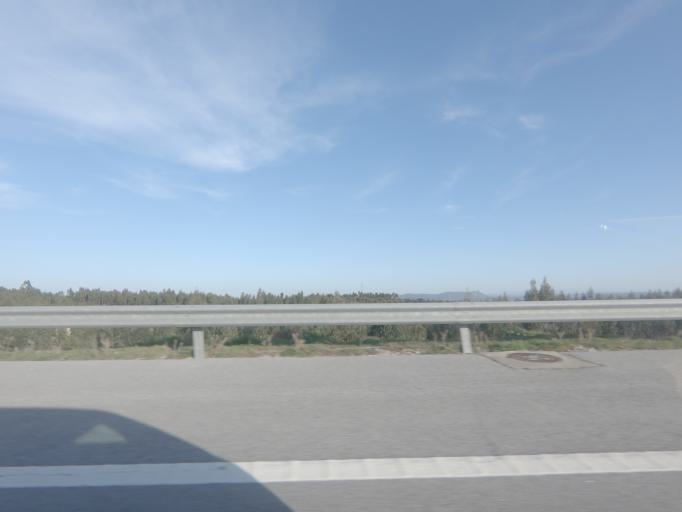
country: PT
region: Portalegre
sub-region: Nisa
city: Nisa
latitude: 39.6406
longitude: -7.7443
